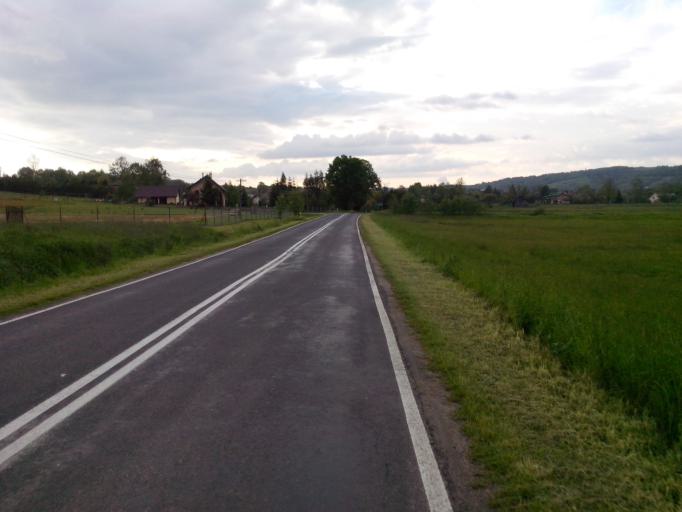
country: PL
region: Subcarpathian Voivodeship
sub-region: Powiat strzyzowski
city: Strzyzow
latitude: 49.8260
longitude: 21.8284
